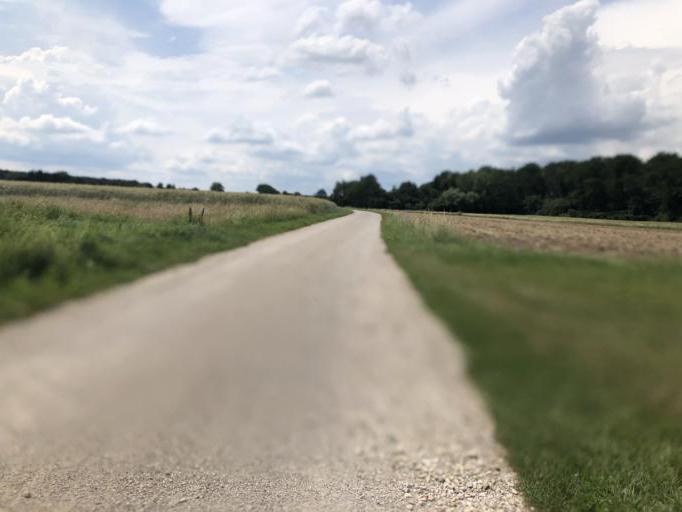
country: DE
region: Bavaria
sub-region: Regierungsbezirk Mittelfranken
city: Hessdorf
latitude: 49.6257
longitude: 10.9308
